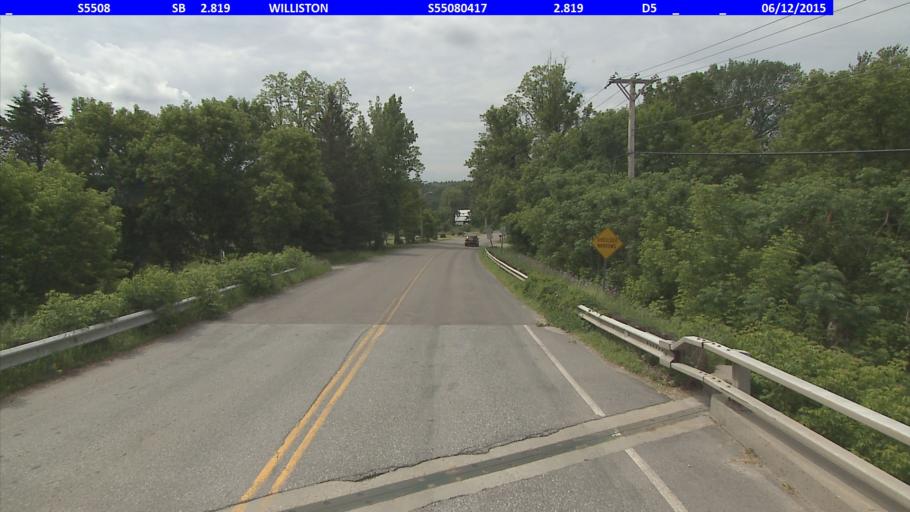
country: US
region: Vermont
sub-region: Chittenden County
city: Williston
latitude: 44.4707
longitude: -73.0440
